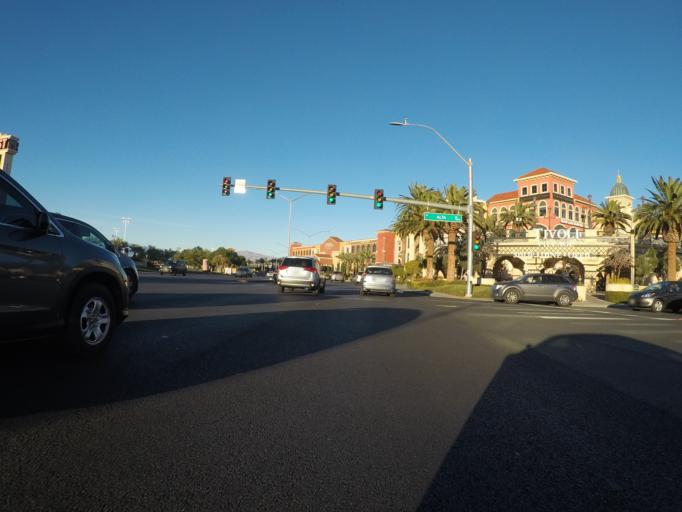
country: US
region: Nevada
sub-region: Clark County
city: Summerlin South
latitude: 36.1666
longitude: -115.2880
